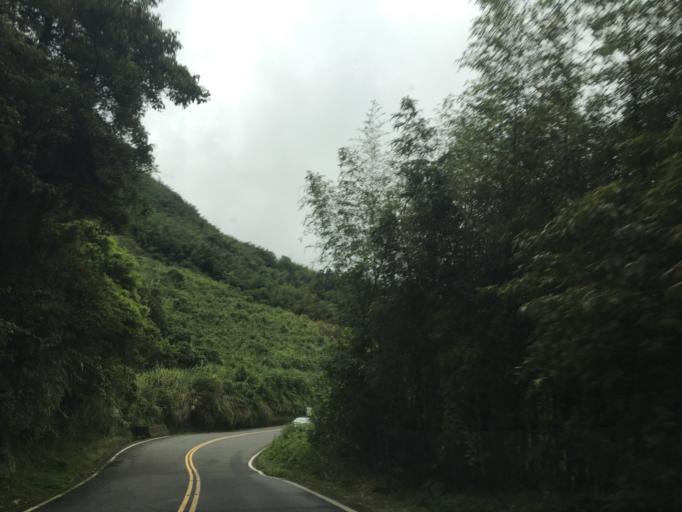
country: TW
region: Taiwan
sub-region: Chiayi
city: Jiayi Shi
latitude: 23.4952
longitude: 120.7002
